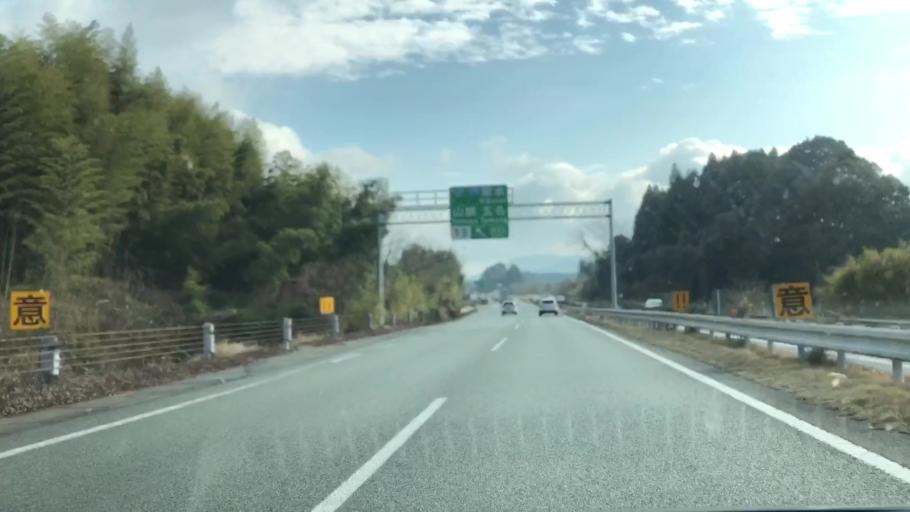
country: JP
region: Kumamoto
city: Tamana
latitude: 32.9901
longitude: 130.6034
